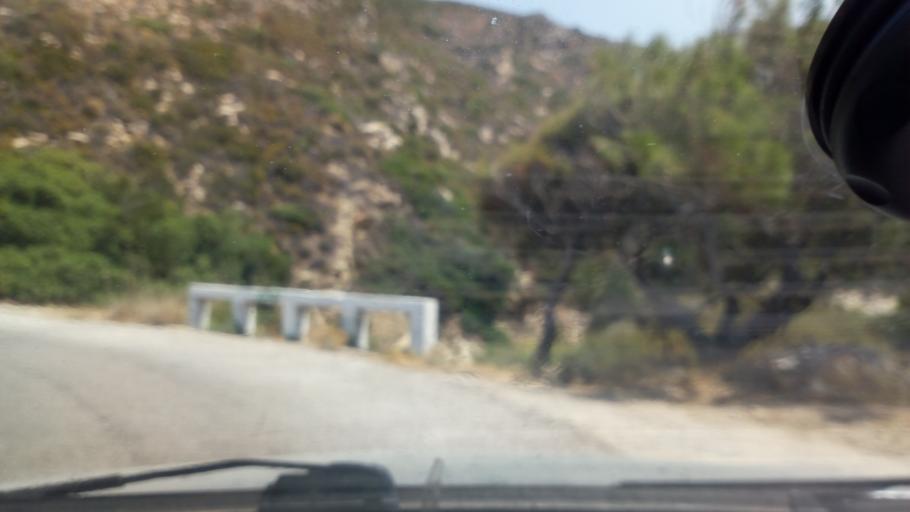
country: GR
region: North Aegean
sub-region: Nomos Samou
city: Agios Kirykos
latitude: 37.6330
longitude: 26.1218
